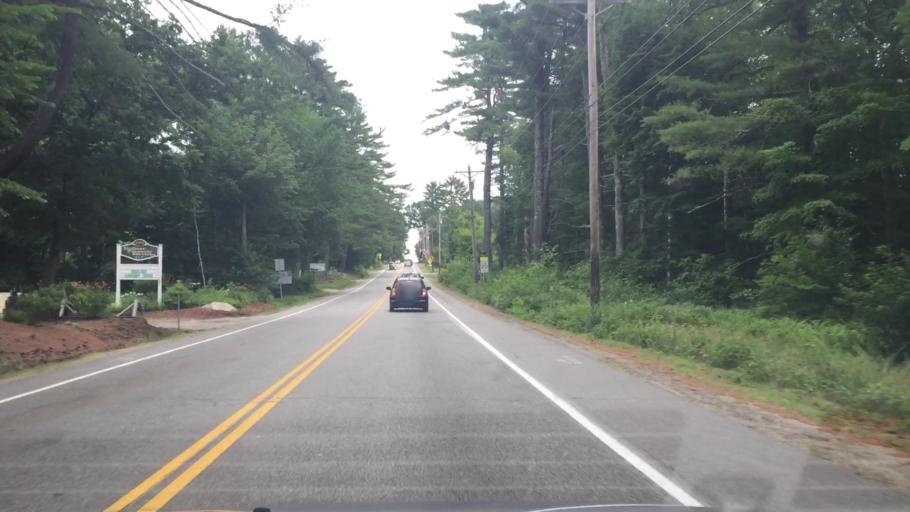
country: US
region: New Hampshire
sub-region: Carroll County
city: Moultonborough
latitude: 43.7484
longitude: -71.4032
